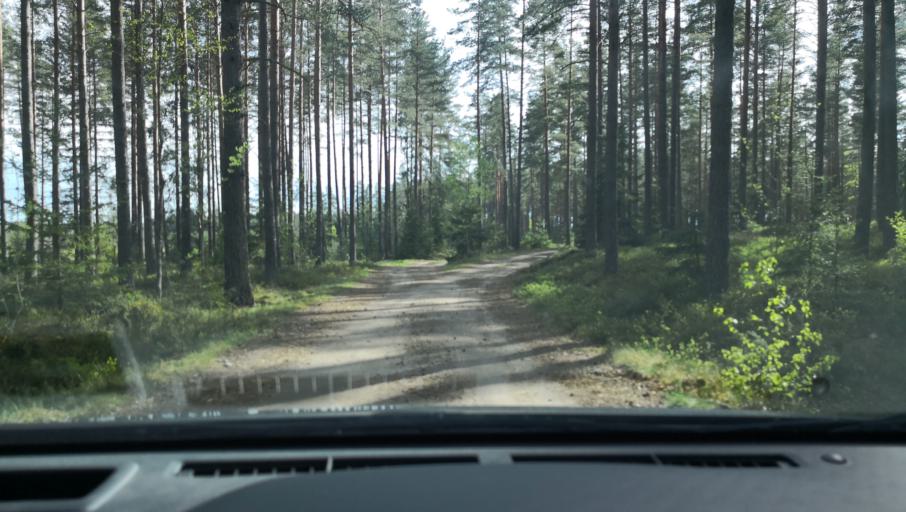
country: SE
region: OErebro
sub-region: Askersunds Kommun
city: Asbro
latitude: 59.0259
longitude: 15.0545
